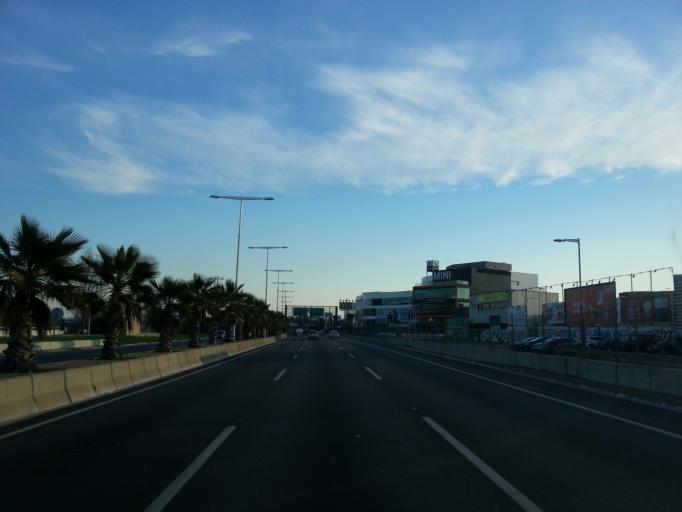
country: ES
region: Catalonia
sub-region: Provincia de Barcelona
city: Sant Adria de Besos
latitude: 41.4341
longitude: 2.2100
